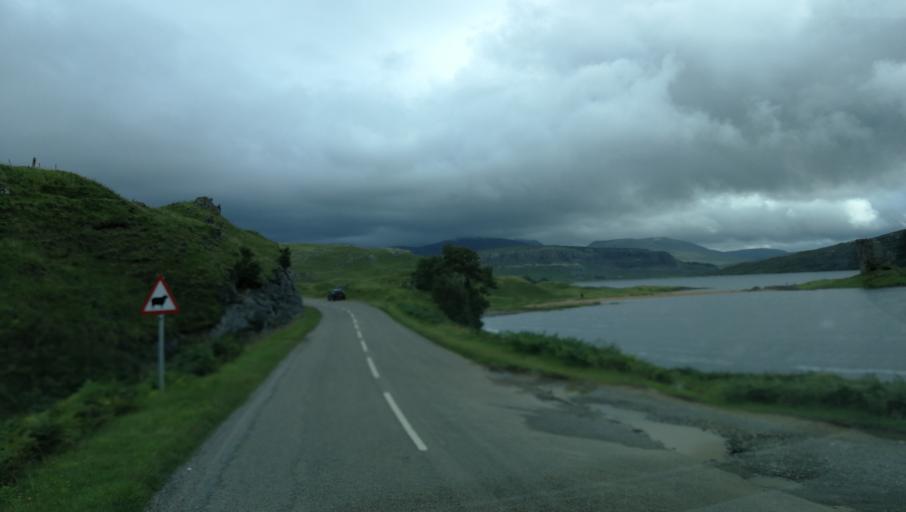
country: GB
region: Scotland
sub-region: Highland
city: Ullapool
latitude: 58.1692
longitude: -4.9942
